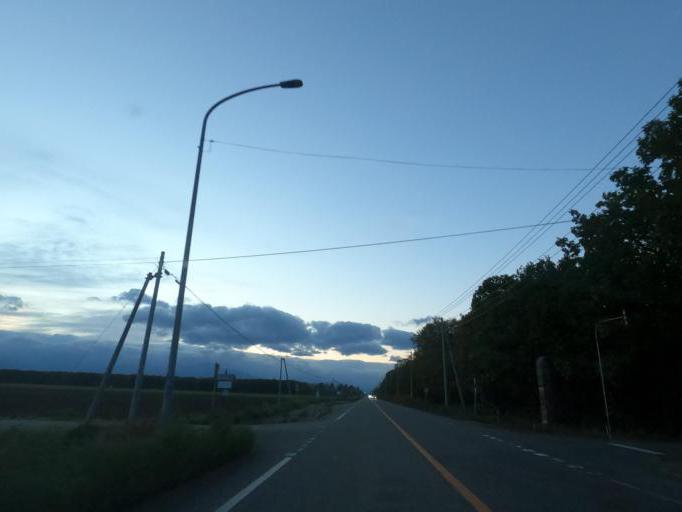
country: JP
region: Hokkaido
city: Obihiro
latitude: 42.6765
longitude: 143.1631
